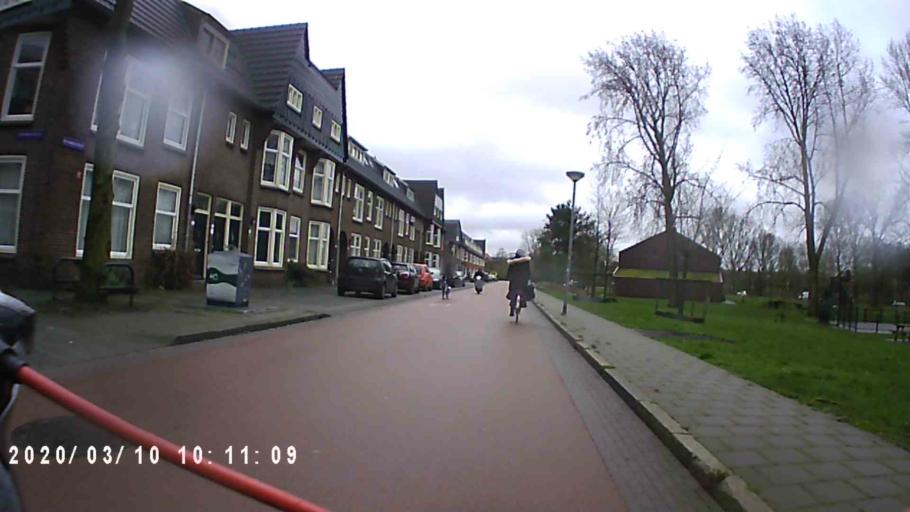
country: NL
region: Groningen
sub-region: Gemeente Groningen
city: Korrewegwijk
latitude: 53.2282
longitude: 6.5496
